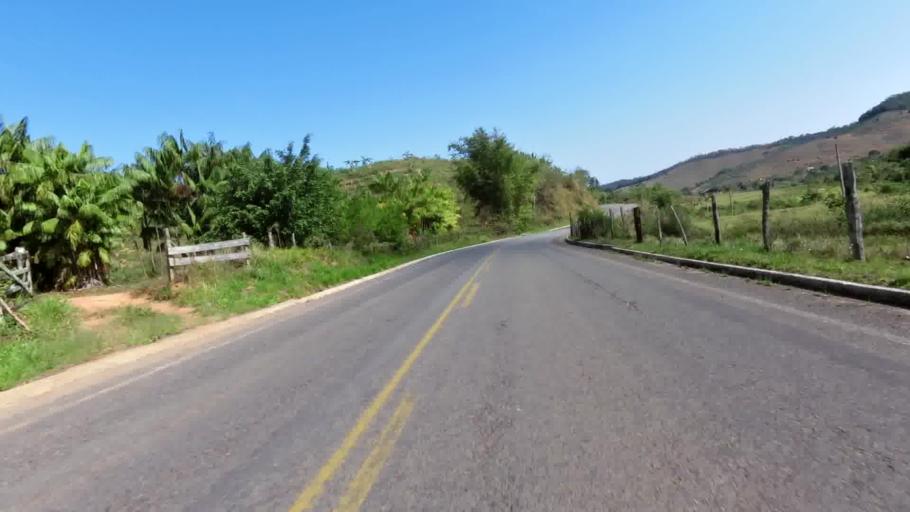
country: BR
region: Espirito Santo
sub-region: Alfredo Chaves
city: Alfredo Chaves
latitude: -20.5259
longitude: -40.7793
